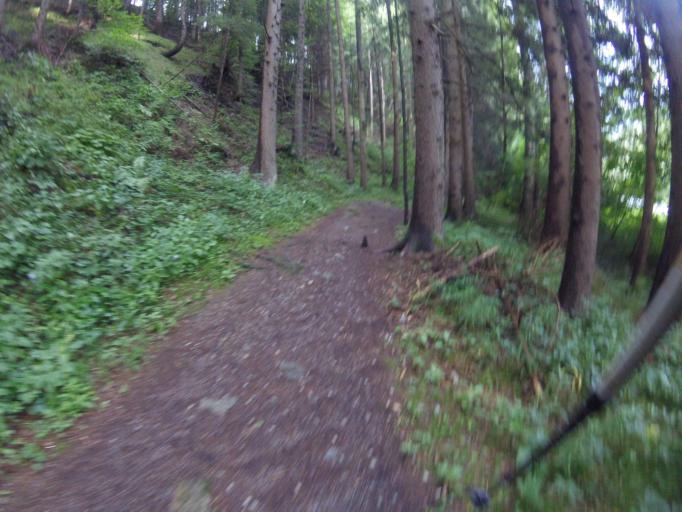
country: SK
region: Zilinsky
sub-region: Okres Zilina
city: Terchova
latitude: 49.2333
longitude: 19.0603
